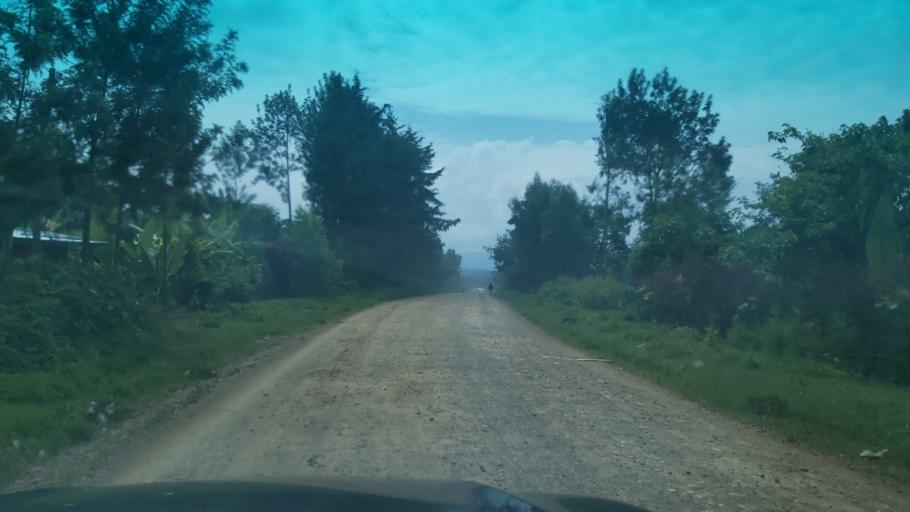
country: ET
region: Oromiya
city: Jima
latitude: 7.7381
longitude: 36.7716
